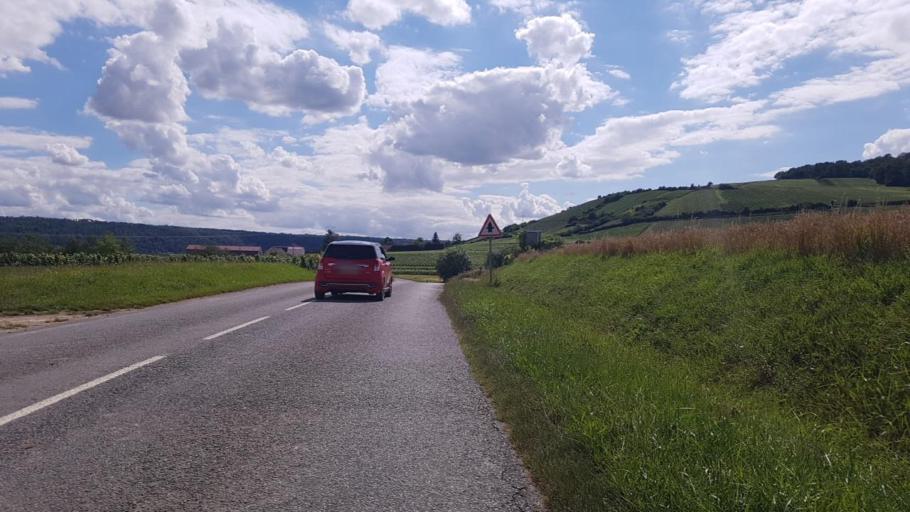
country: FR
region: Champagne-Ardenne
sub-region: Departement de la Marne
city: Dormans
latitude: 49.0715
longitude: 3.5986
